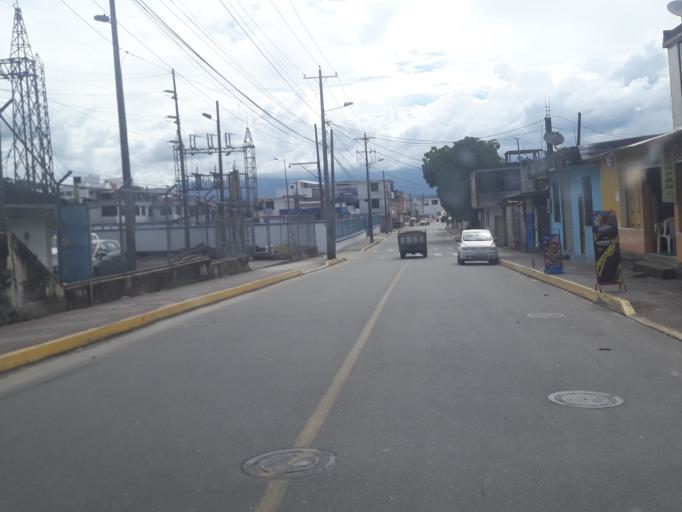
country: EC
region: Napo
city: Tena
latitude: -1.0071
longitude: -77.8113
